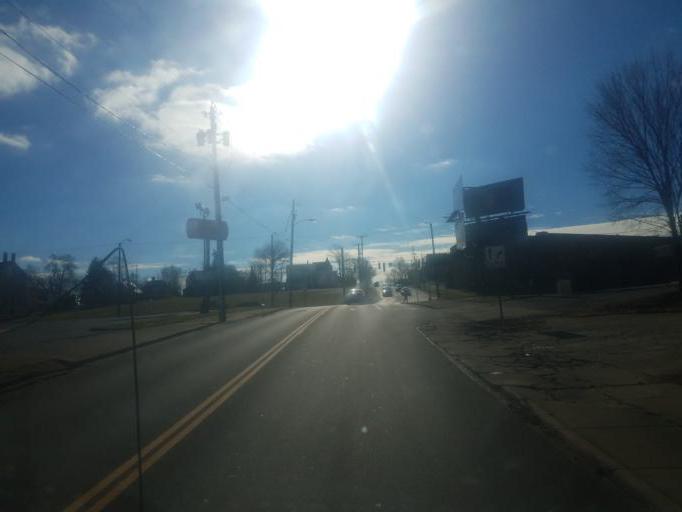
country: US
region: Ohio
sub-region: Richland County
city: Mansfield
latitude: 40.7596
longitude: -82.5230
